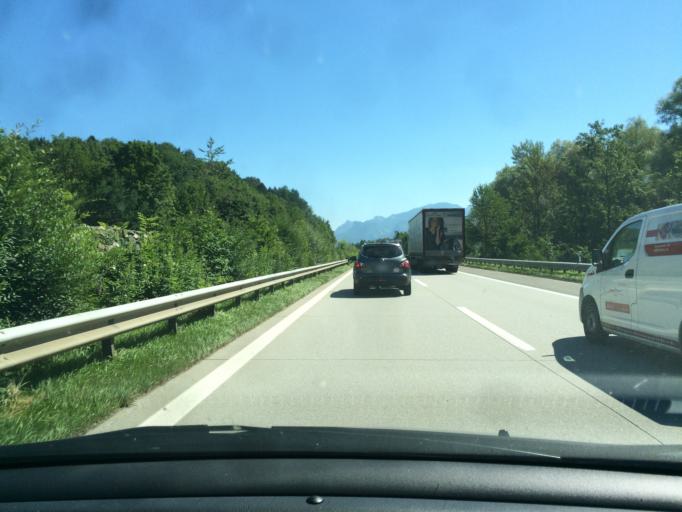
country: CH
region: Saint Gallen
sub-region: Wahlkreis Rheintal
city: Ruthi
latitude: 47.2772
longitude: 9.5370
